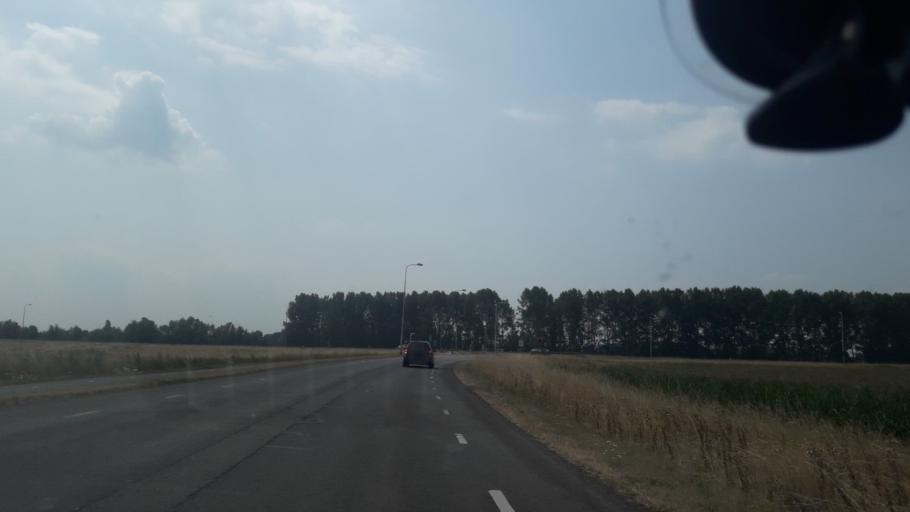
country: NL
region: Gelderland
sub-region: Gemeente Rheden
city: Ellecom
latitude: 52.0304
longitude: 6.1081
